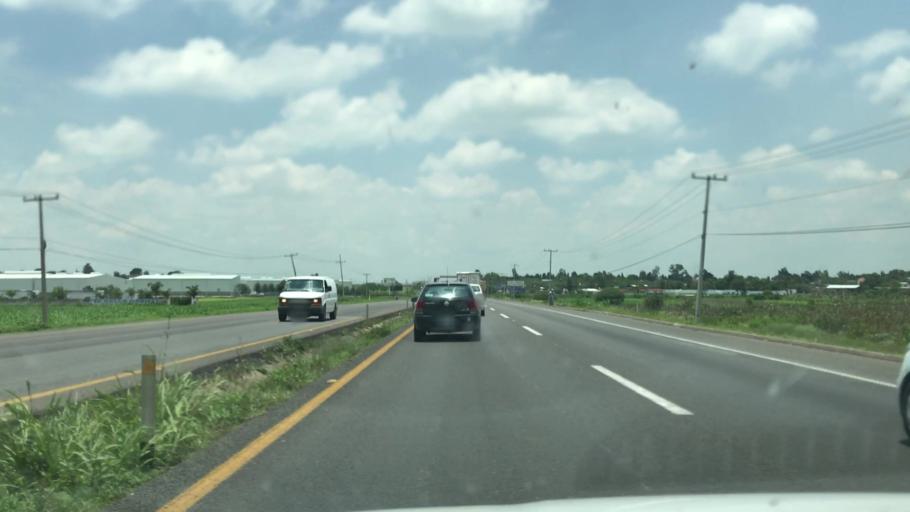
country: MX
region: Guanajuato
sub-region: Irapuato
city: Colonia Morelos de Guadalupe de Rivera
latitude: 20.5756
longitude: -101.4388
